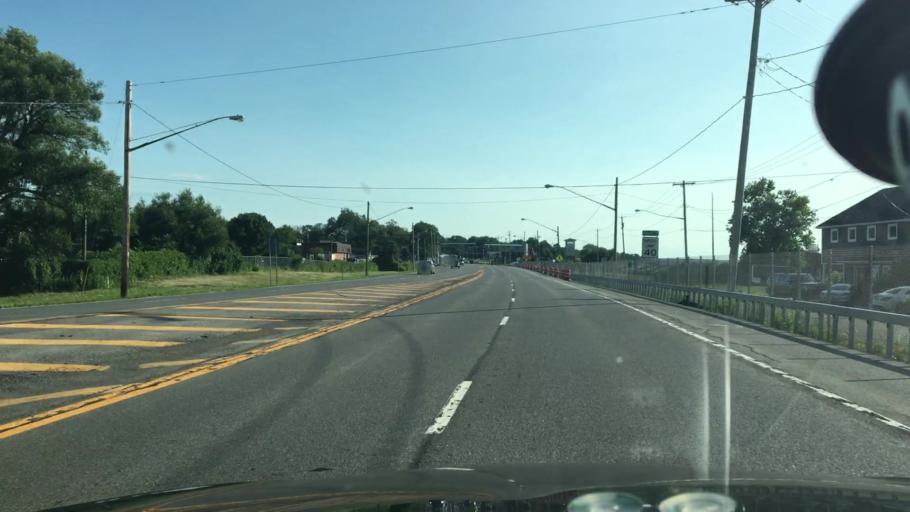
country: US
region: New York
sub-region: Erie County
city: Blasdell
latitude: 42.7758
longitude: -78.8614
